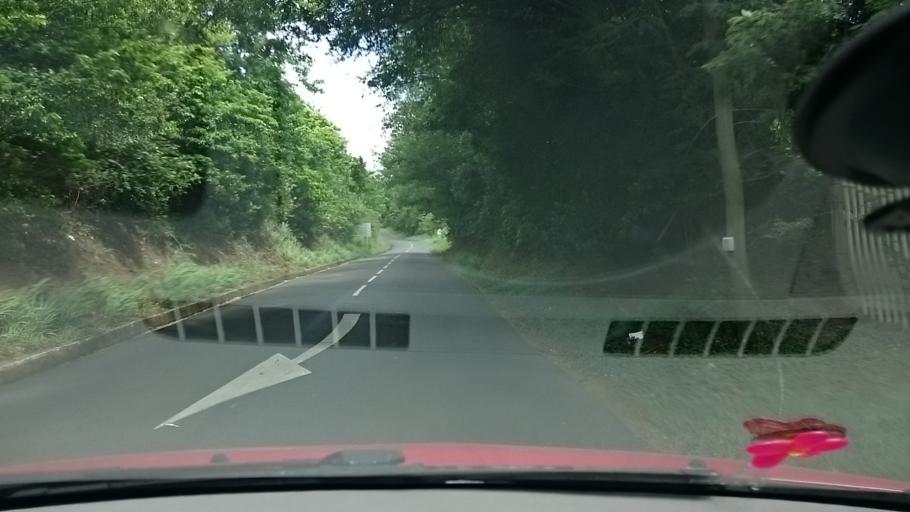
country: MQ
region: Martinique
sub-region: Martinique
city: La Trinite
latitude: 14.7553
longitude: -60.9255
